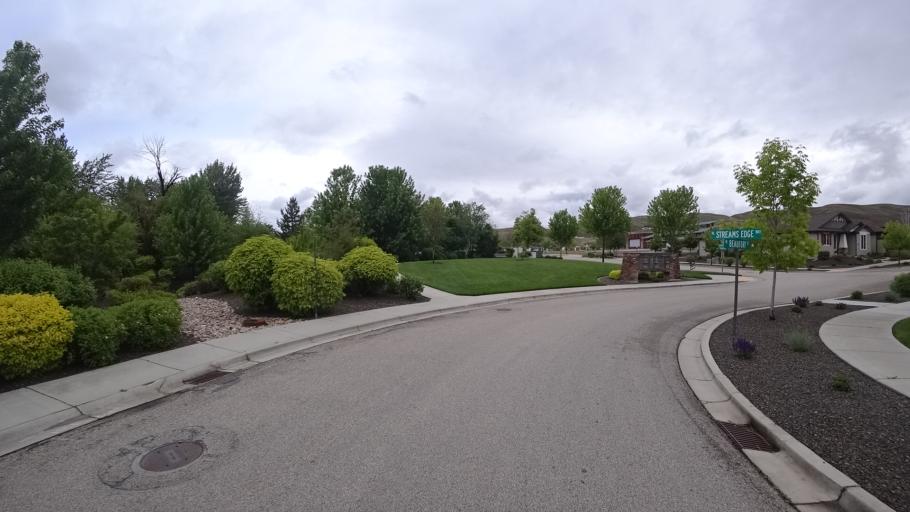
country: US
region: Idaho
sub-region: Ada County
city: Eagle
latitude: 43.7717
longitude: -116.2643
